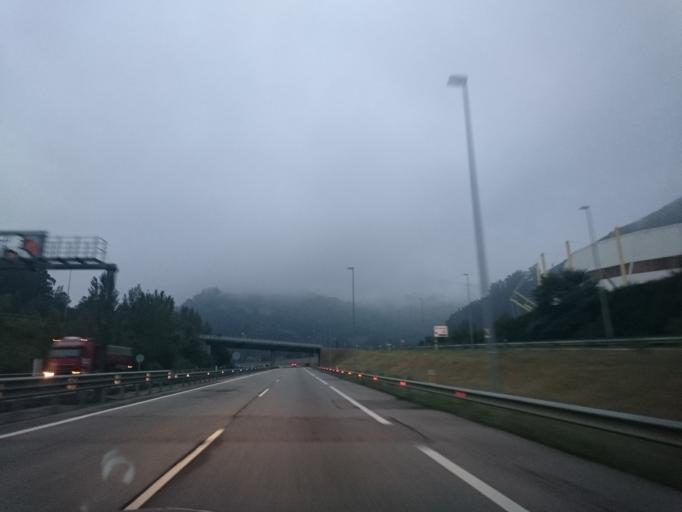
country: ES
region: Asturias
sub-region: Province of Asturias
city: Mieres
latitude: 43.2738
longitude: -5.8080
